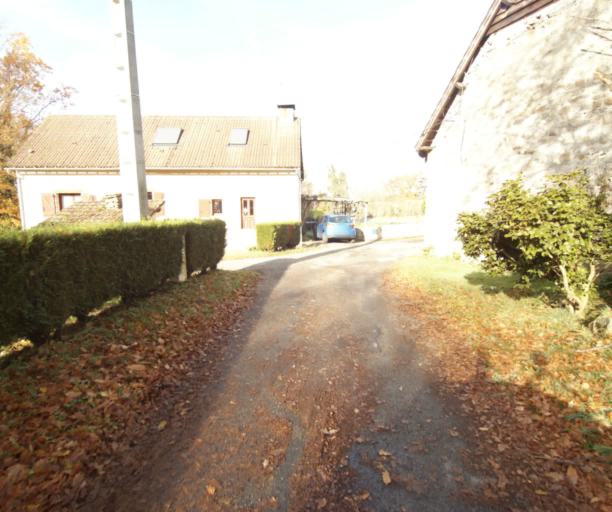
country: FR
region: Limousin
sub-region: Departement de la Correze
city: Sainte-Fortunade
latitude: 45.2202
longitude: 1.7461
